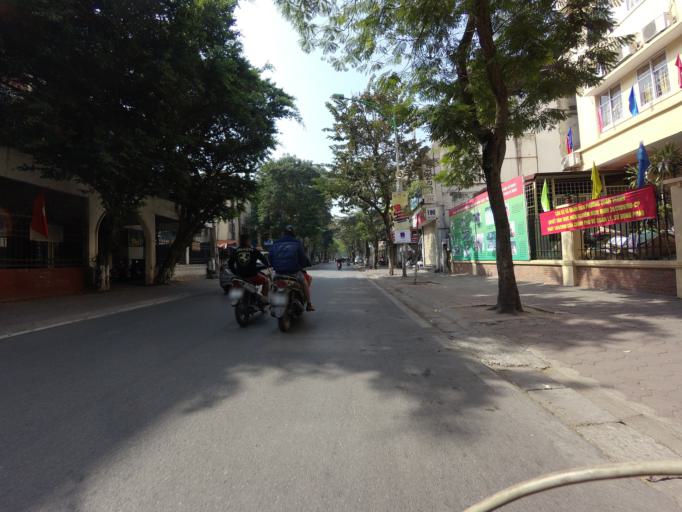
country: VN
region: Ha Noi
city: Hanoi
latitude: 21.0427
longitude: 105.8383
